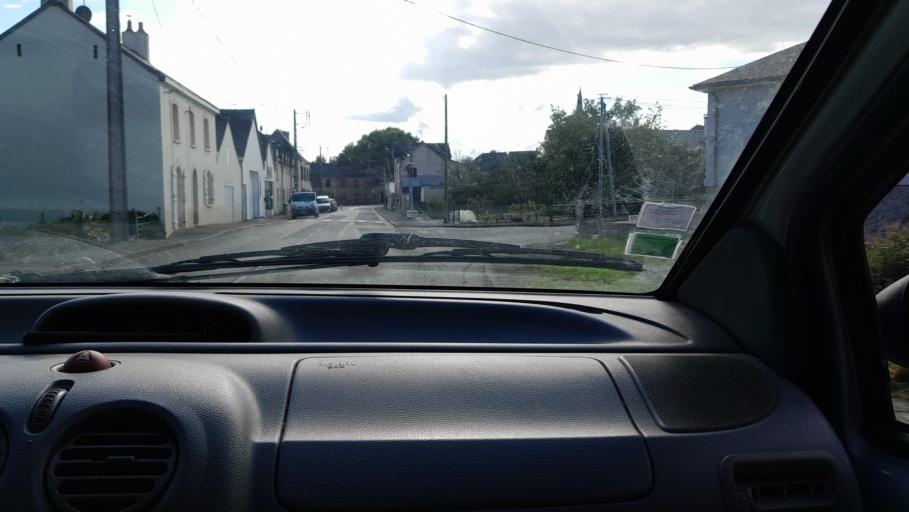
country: FR
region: Pays de la Loire
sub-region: Departement de la Mayenne
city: Loiron
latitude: 48.0072
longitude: -0.9577
